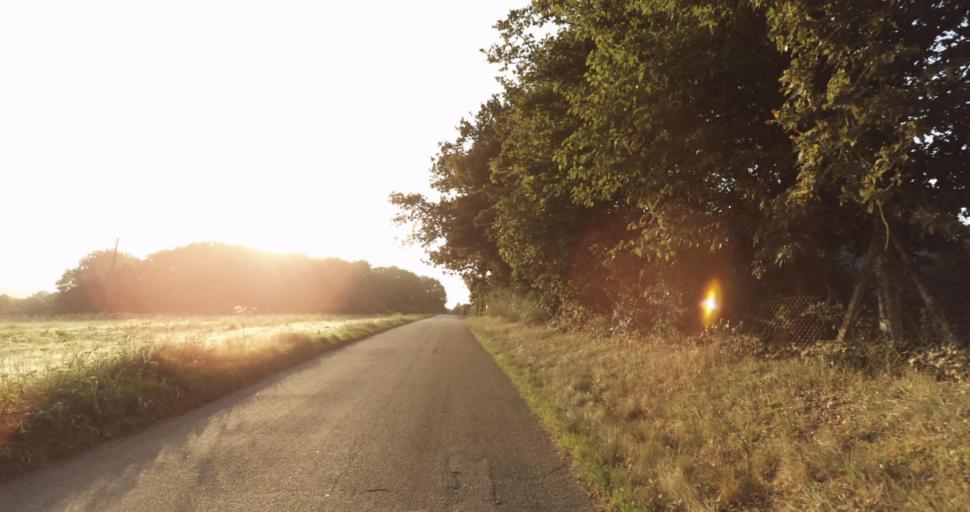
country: FR
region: Haute-Normandie
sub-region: Departement de l'Eure
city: Marcilly-sur-Eure
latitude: 48.7872
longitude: 1.3382
